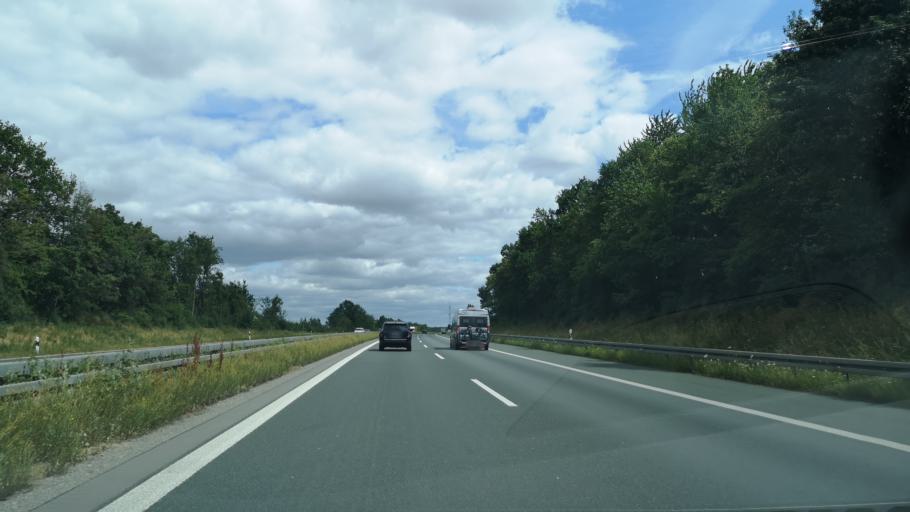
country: DE
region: Bavaria
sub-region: Regierungsbezirk Unterfranken
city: Werneck
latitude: 49.9734
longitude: 10.0359
